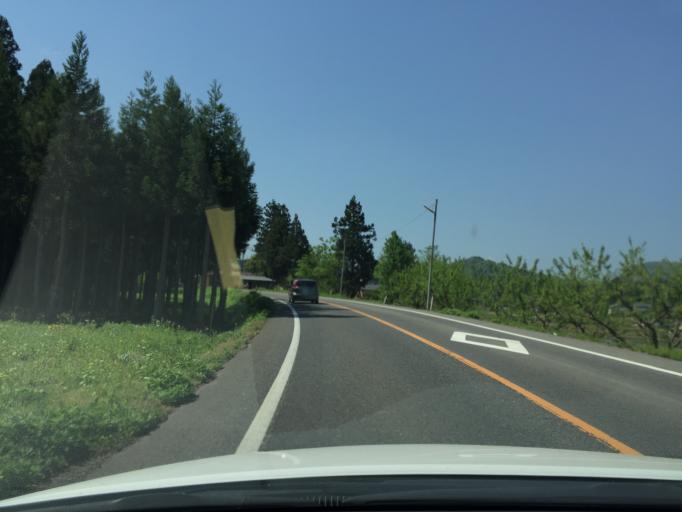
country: JP
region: Niigata
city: Muramatsu
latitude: 37.6641
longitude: 139.1382
